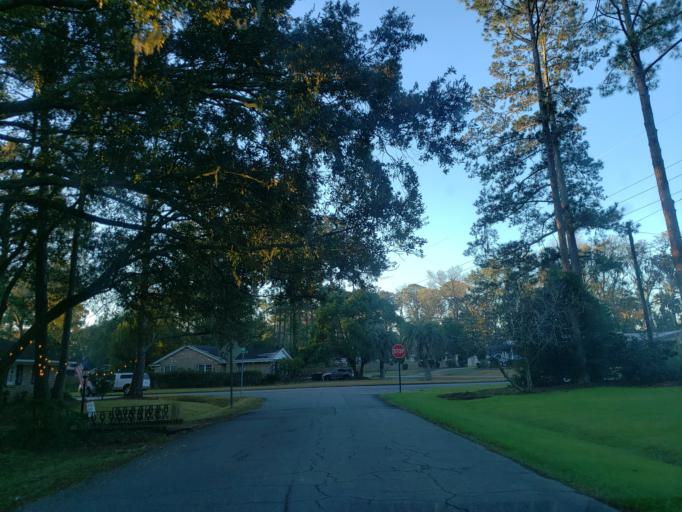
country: US
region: Georgia
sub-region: Chatham County
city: Thunderbolt
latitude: 32.0173
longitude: -81.0837
